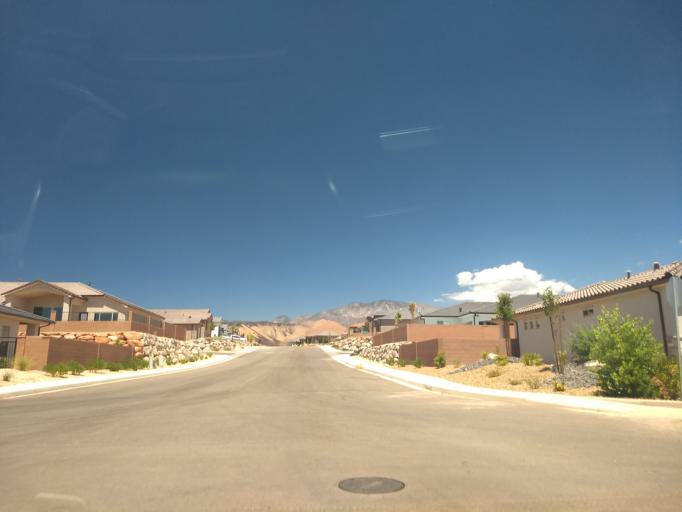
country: US
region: Utah
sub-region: Washington County
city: Washington
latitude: 37.1565
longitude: -113.5216
